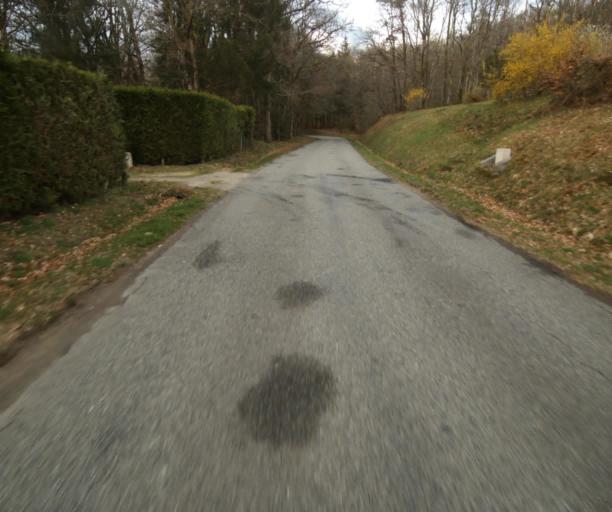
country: FR
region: Limousin
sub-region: Departement de la Correze
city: Argentat
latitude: 45.2241
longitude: 1.9780
